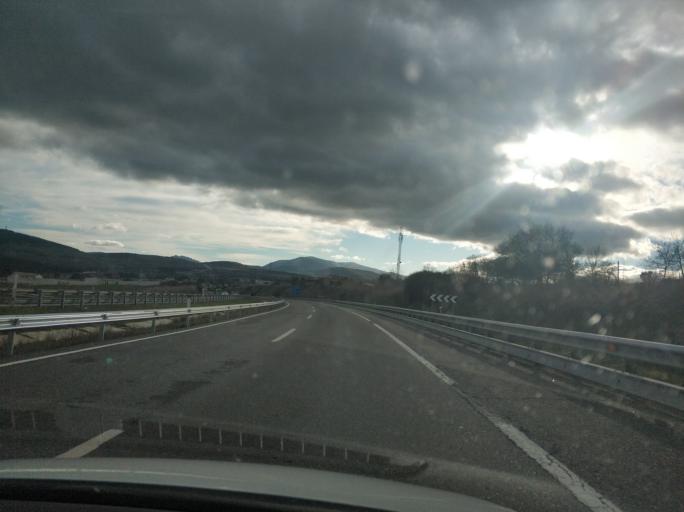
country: ES
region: Madrid
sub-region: Provincia de Madrid
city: Gascones
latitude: 41.0076
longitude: -3.6372
